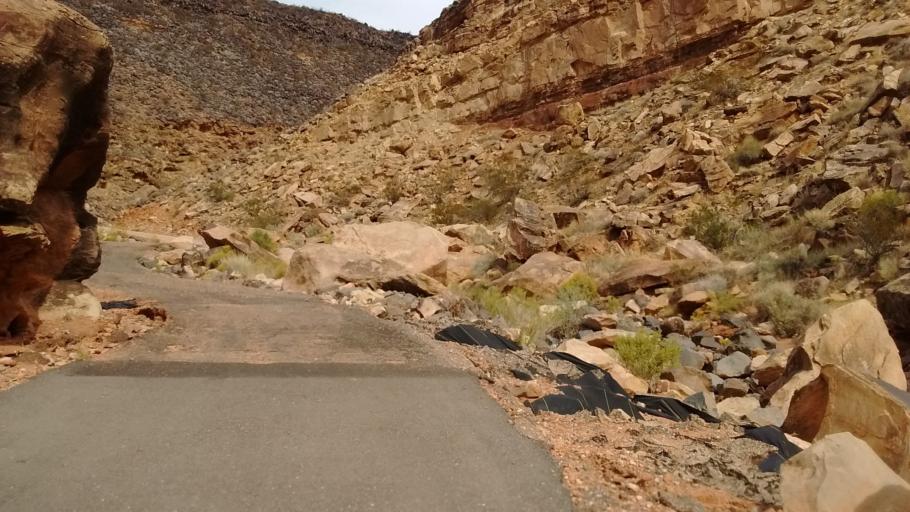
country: US
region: Utah
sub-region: Washington County
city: Washington
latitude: 37.1268
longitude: -113.4787
